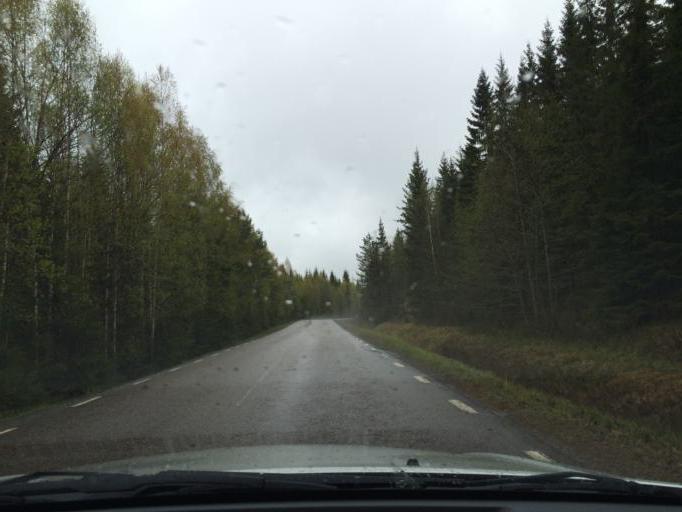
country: SE
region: Dalarna
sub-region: Ludvika Kommun
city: Abborrberget
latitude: 60.0656
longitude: 14.8302
